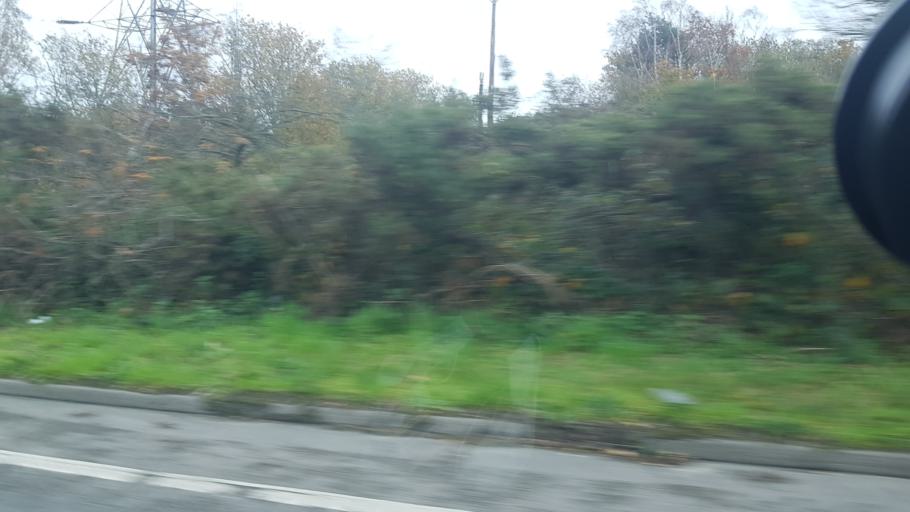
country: GB
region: England
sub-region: Hampshire
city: Fleet
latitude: 51.3037
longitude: -0.7974
